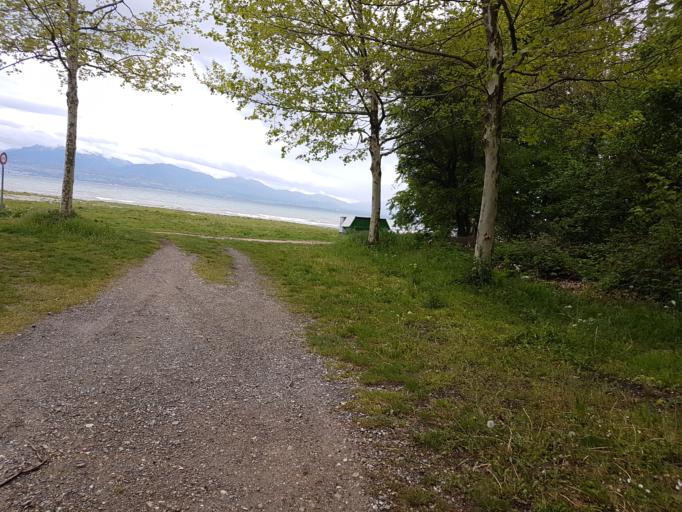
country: CH
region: Vaud
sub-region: Morges District
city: Preverenges
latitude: 46.5085
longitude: 6.5445
